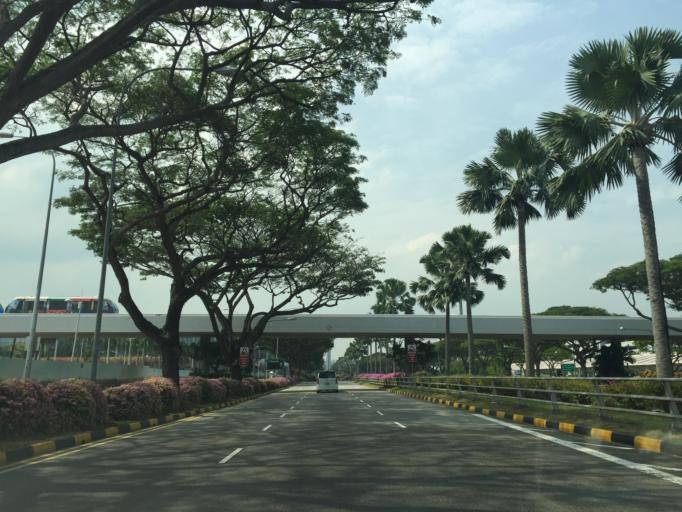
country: SG
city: Singapore
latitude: 1.3515
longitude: 103.9860
